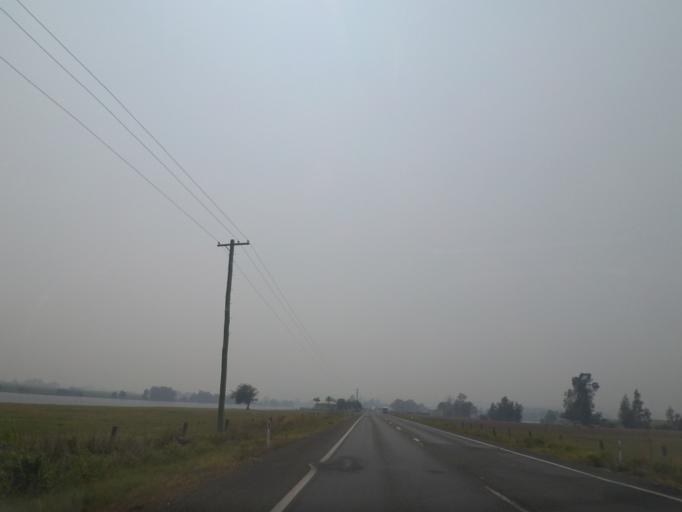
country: AU
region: New South Wales
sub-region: Clarence Valley
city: Maclean
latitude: -29.5653
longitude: 153.1195
